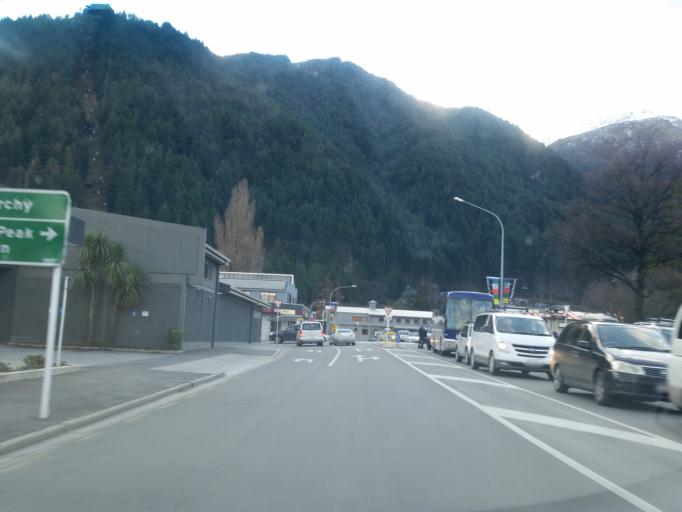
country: NZ
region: Otago
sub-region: Queenstown-Lakes District
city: Queenstown
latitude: -45.0306
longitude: 168.6621
